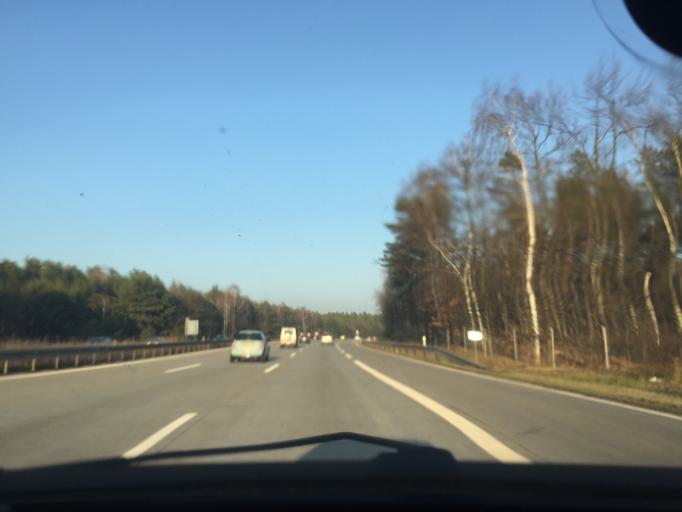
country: DE
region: Berlin
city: Wannsee
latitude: 52.3862
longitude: 13.1540
